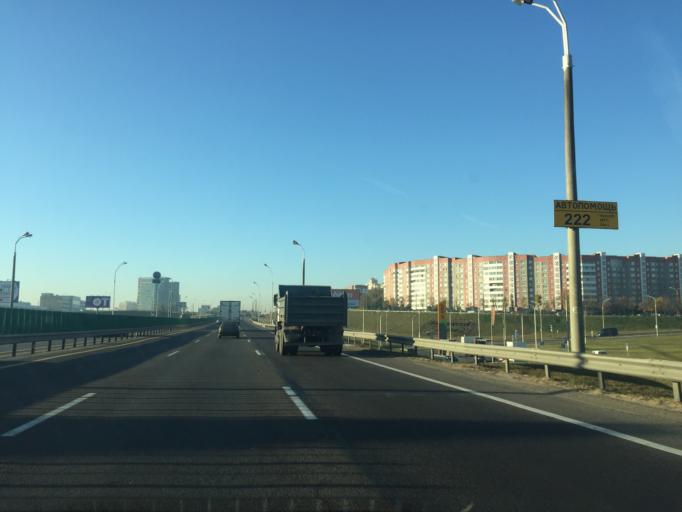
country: BY
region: Minsk
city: Vyaliki Trastsyanets
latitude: 53.8705
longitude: 27.6917
